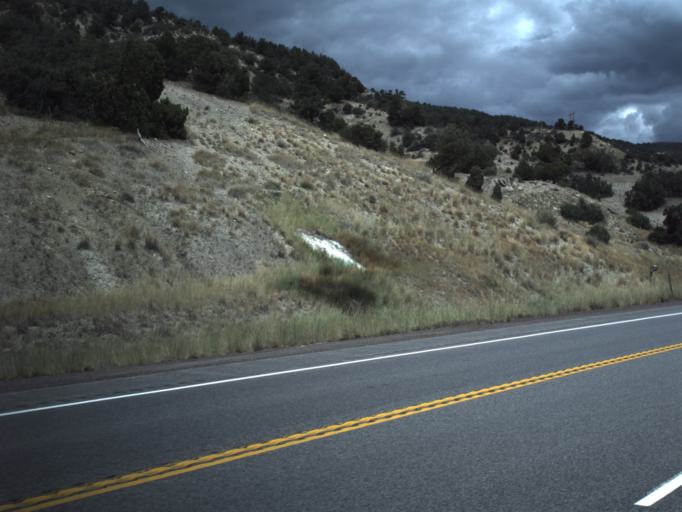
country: US
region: Utah
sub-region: Carbon County
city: Helper
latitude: 39.9335
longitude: -111.1579
